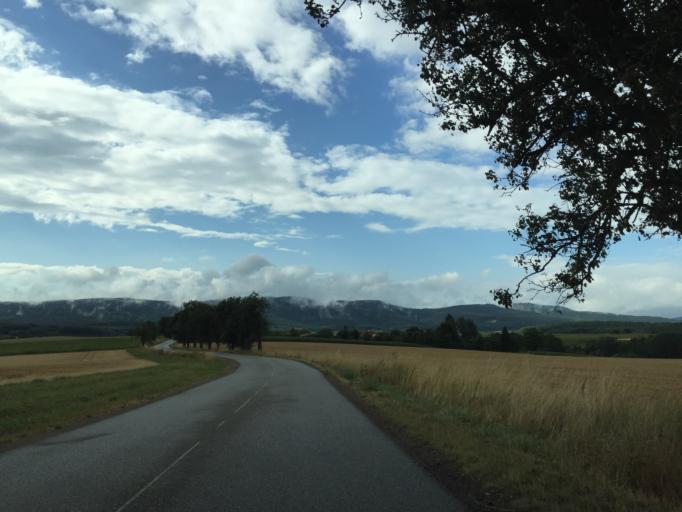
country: FR
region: Alsace
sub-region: Departement du Bas-Rhin
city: Soultz-sous-Forets
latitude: 48.9776
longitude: 7.9108
